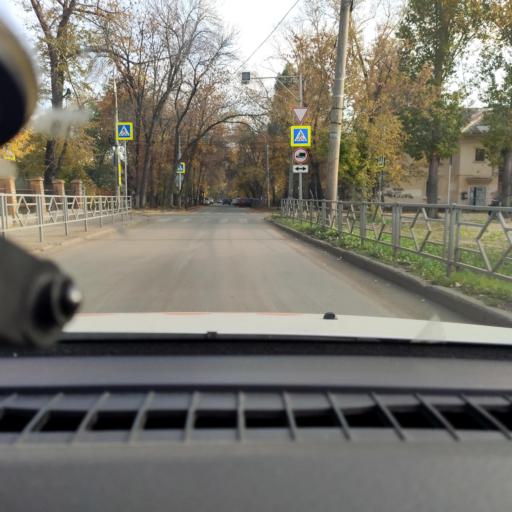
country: RU
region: Samara
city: Samara
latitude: 53.1189
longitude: 50.0780
